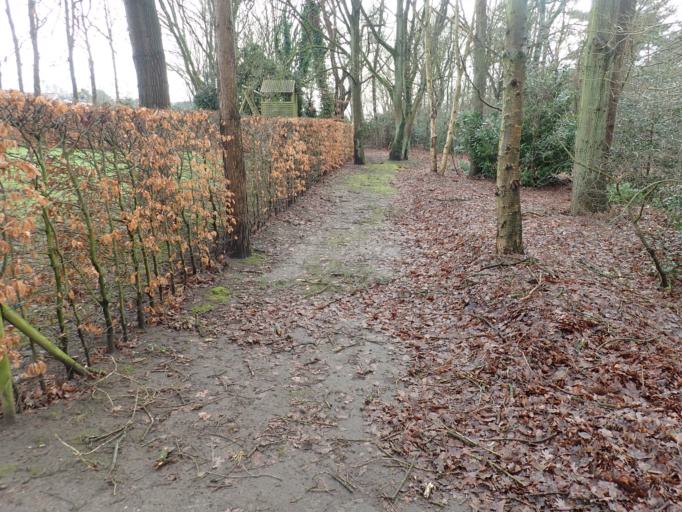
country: BE
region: Flanders
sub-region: Provincie Antwerpen
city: Nijlen
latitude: 51.1658
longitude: 4.6454
